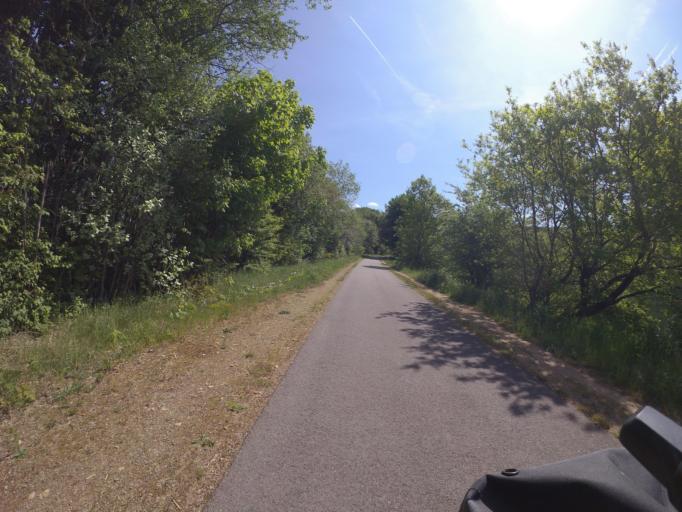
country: BE
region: Wallonia
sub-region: Province de Liege
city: Butgenbach
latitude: 50.4335
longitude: 6.2045
